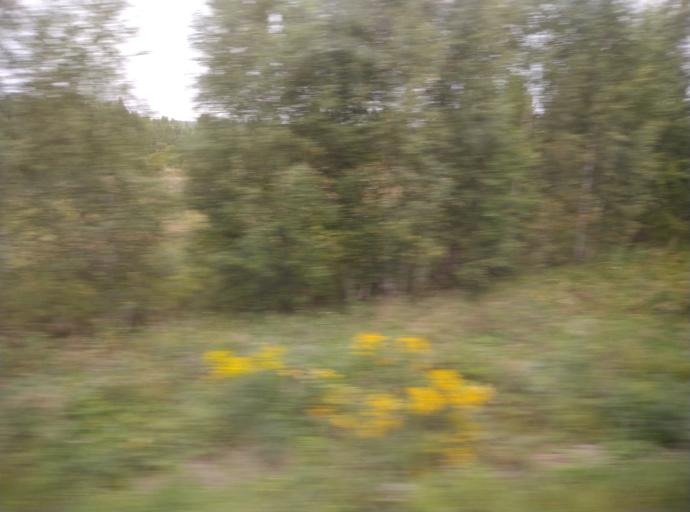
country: RU
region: Kostroma
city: Kosmynino
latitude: 57.5820
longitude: 40.7514
